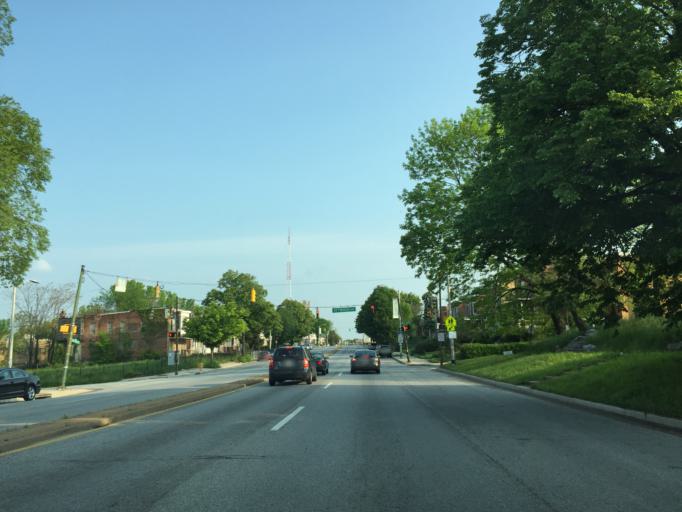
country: US
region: Maryland
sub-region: Baltimore County
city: Lochearn
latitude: 39.3329
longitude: -76.6614
